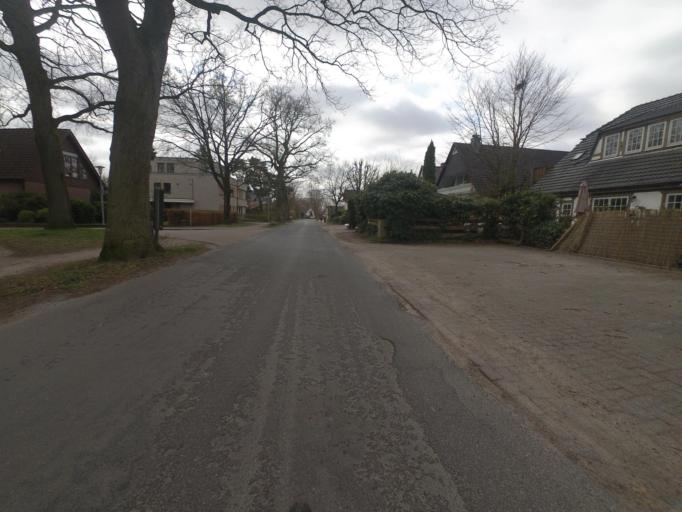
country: DE
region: Lower Saxony
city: Oldenburg
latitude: 53.1347
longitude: 8.1538
